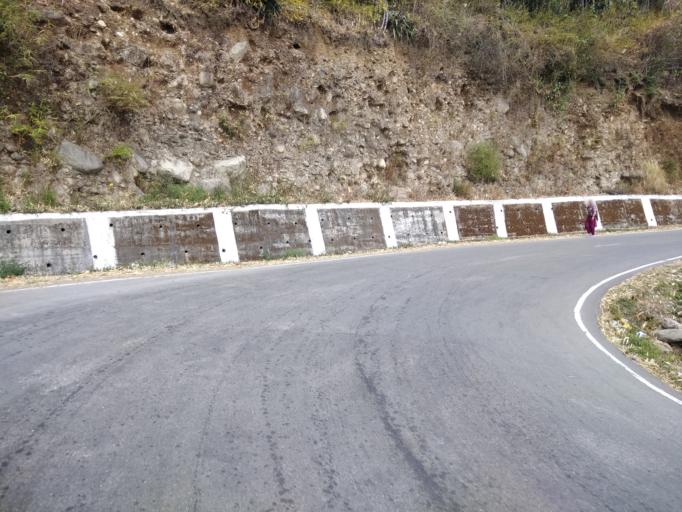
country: IN
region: Himachal Pradesh
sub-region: Kangra
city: Dharmsala
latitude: 32.1605
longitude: 76.4042
